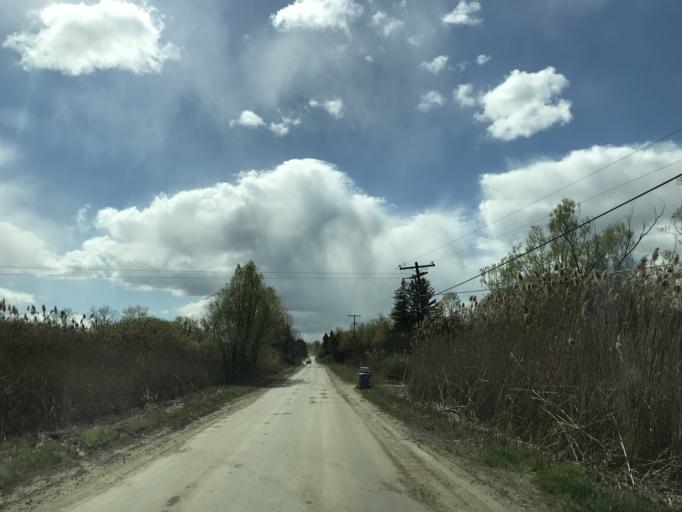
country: US
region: Michigan
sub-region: Oakland County
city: South Lyon
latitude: 42.4038
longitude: -83.6848
